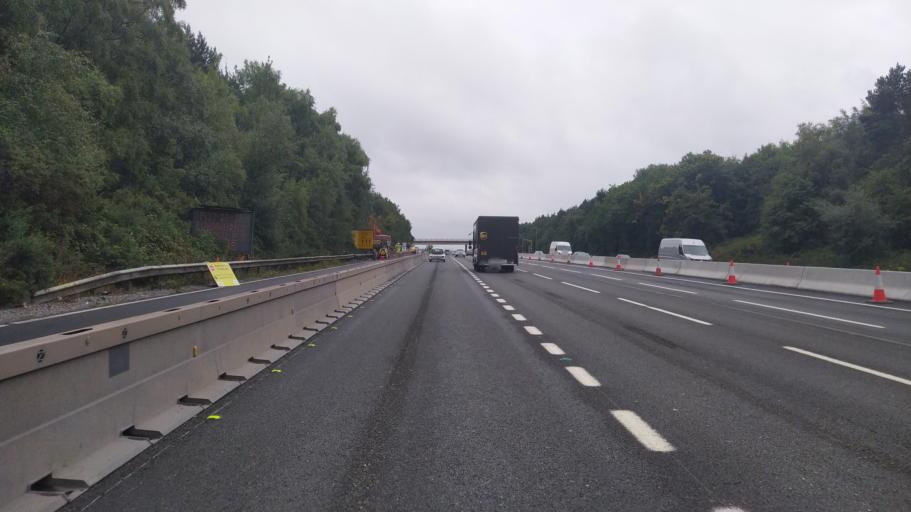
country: GB
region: England
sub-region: Hampshire
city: Hedge End
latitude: 50.9068
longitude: -1.3169
